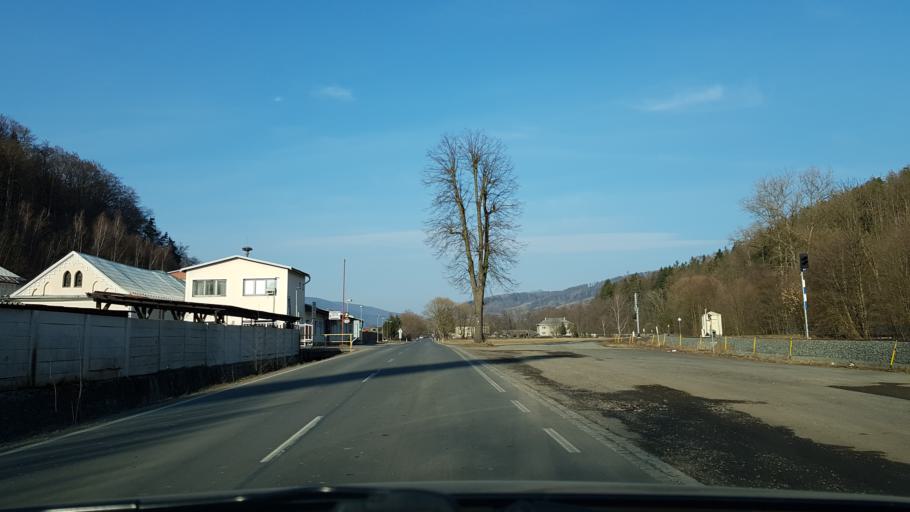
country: CZ
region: Olomoucky
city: Ruda nad Moravou
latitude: 49.9906
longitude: 16.8918
